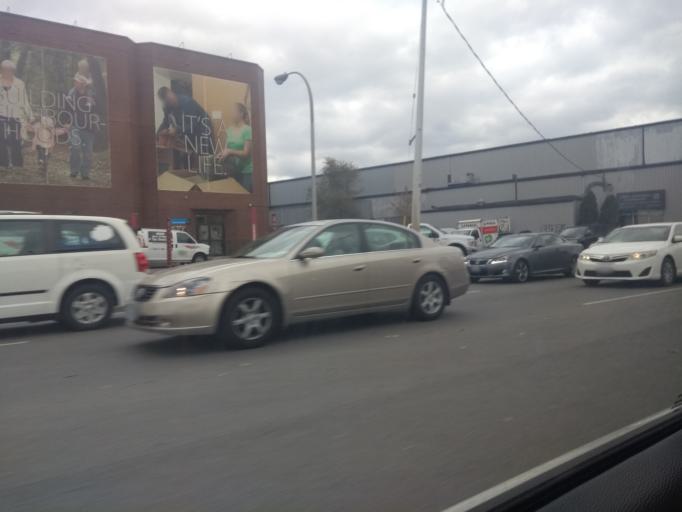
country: CA
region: Ontario
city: Toronto
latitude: 43.6797
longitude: -79.4749
